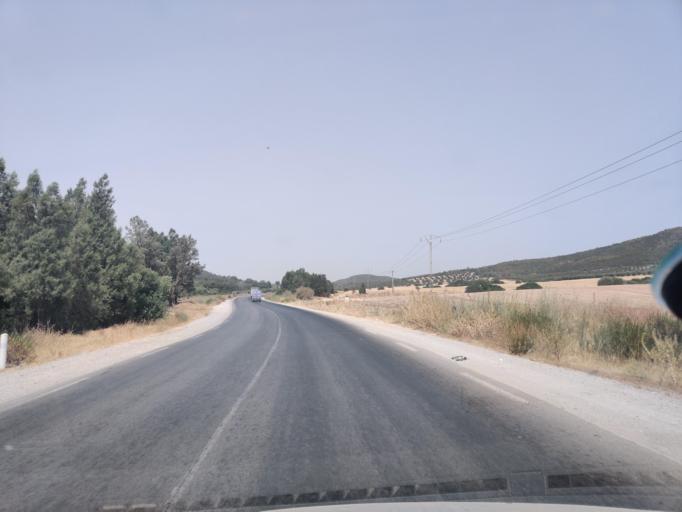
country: TN
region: Tunis
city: Hammam-Lif
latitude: 36.6304
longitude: 10.3931
